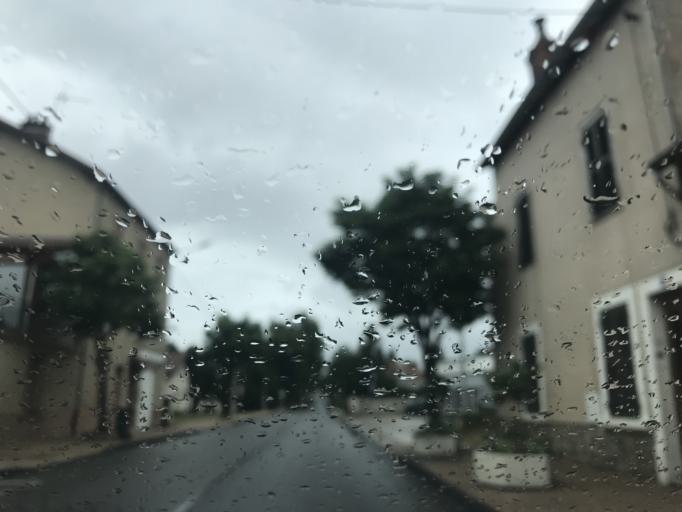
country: FR
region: Auvergne
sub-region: Departement du Puy-de-Dome
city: Ambert
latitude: 45.5548
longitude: 3.7407
